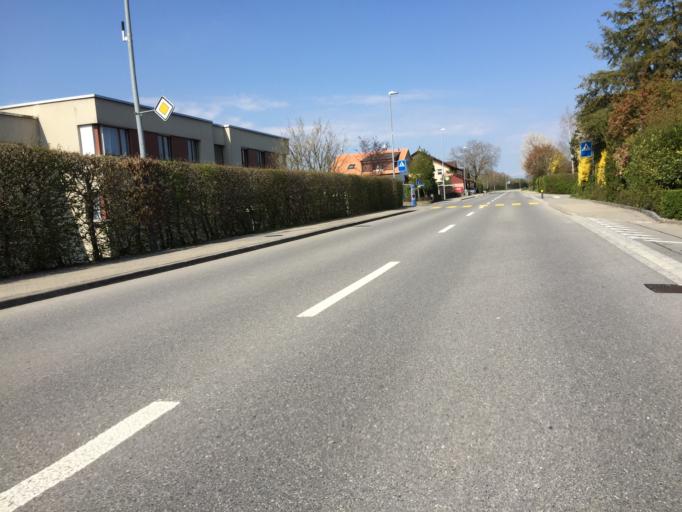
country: CH
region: Bern
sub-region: Bern-Mittelland District
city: Urtenen
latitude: 47.0213
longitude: 7.4927
